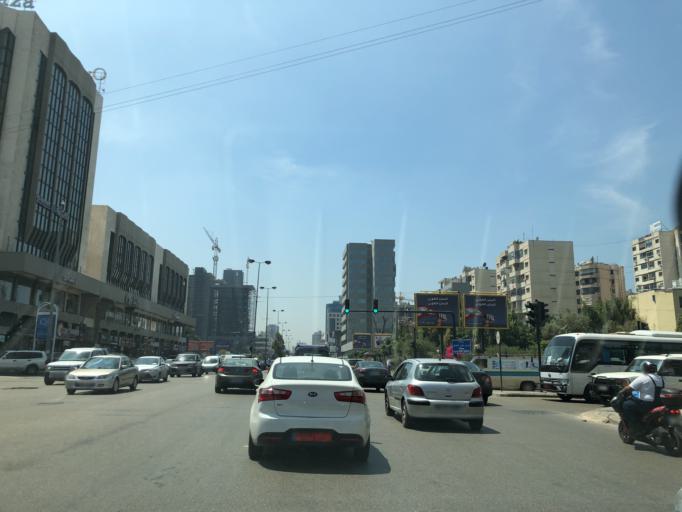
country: LB
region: Mont-Liban
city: Jdaidet el Matn
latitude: 33.8897
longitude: 35.5544
